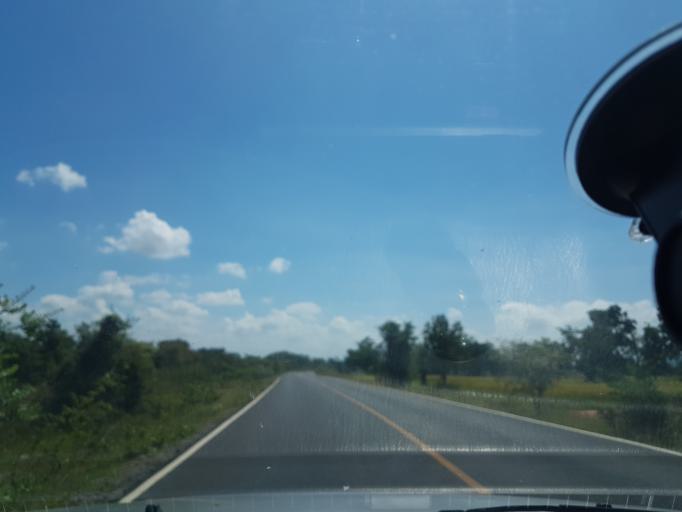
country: TH
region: Lop Buri
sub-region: Amphoe Tha Luang
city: Tha Luang
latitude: 15.0108
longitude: 100.9969
